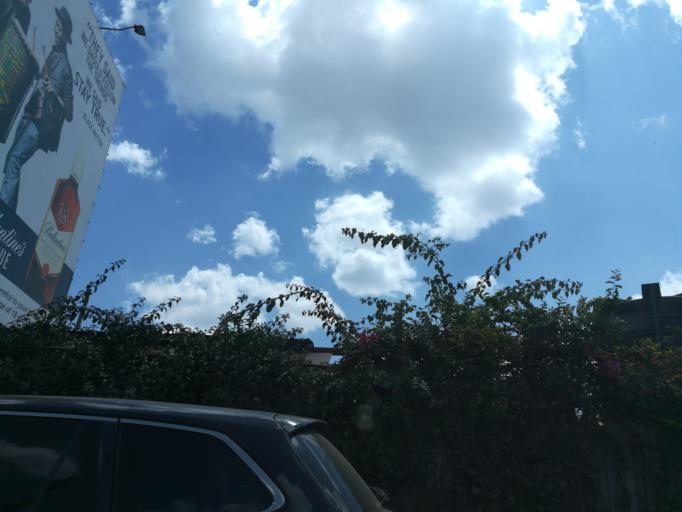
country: KE
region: Nairobi Area
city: Nairobi
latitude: -1.3231
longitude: 36.8035
